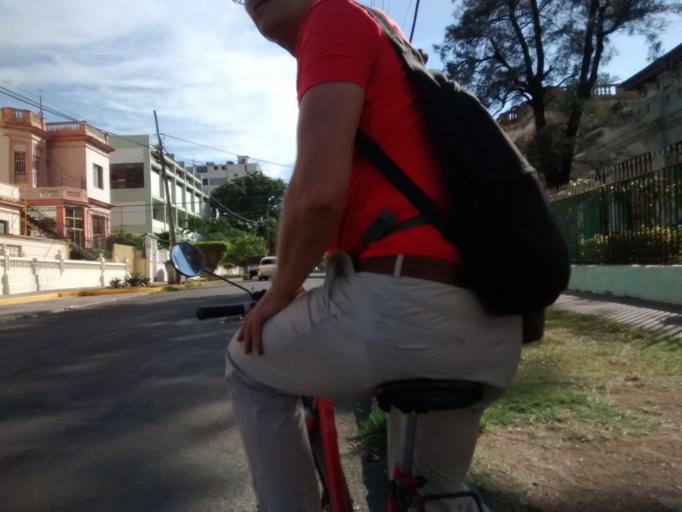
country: CU
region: La Habana
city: Havana
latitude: 23.1421
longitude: -82.3843
